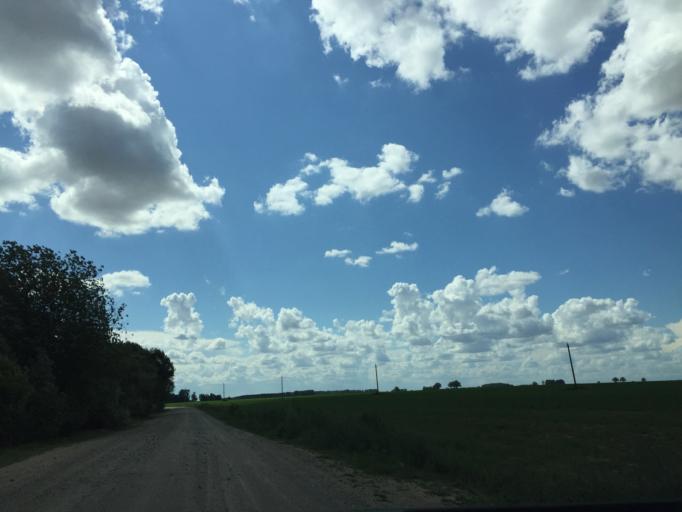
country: LV
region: Rundales
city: Pilsrundale
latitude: 56.3028
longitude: 23.9805
